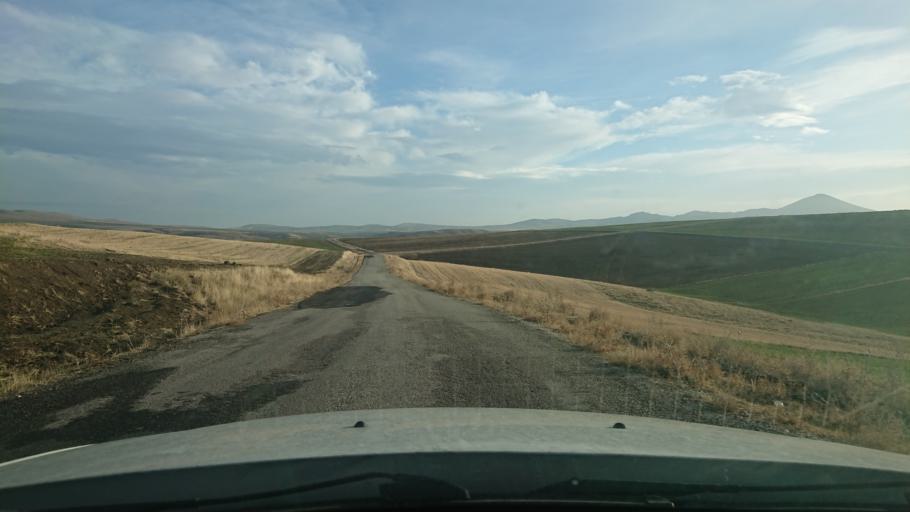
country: TR
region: Aksaray
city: Acipinar
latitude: 38.6669
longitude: 33.8536
